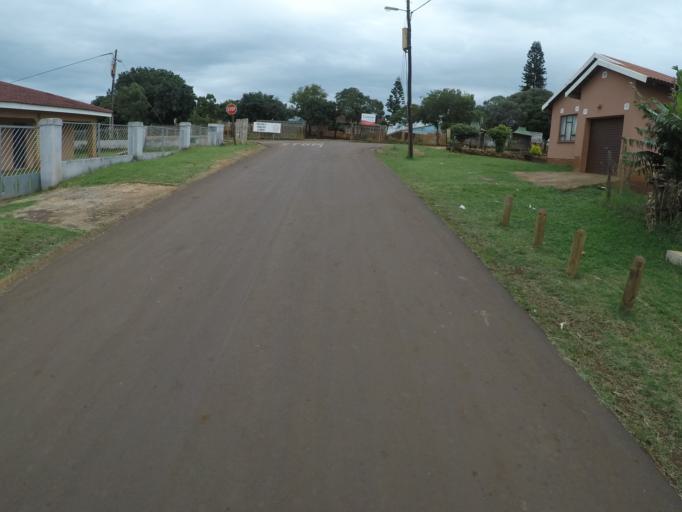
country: ZA
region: KwaZulu-Natal
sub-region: uThungulu District Municipality
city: Empangeni
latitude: -28.7767
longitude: 31.8511
